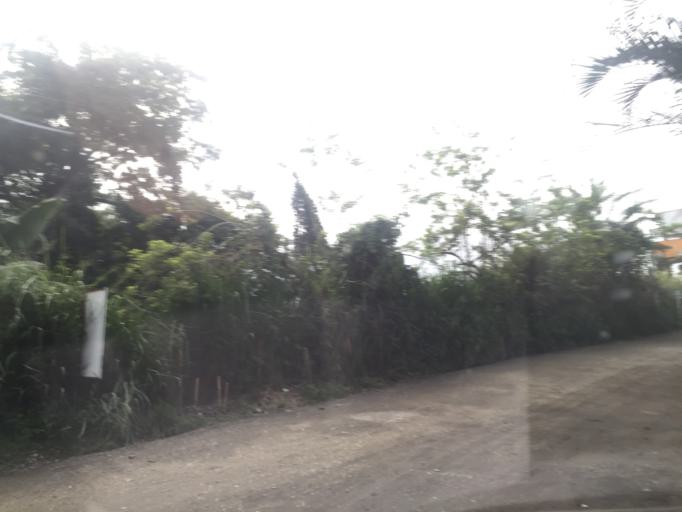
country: CO
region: Quindio
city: La Tebaida
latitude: 4.4570
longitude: -75.7922
